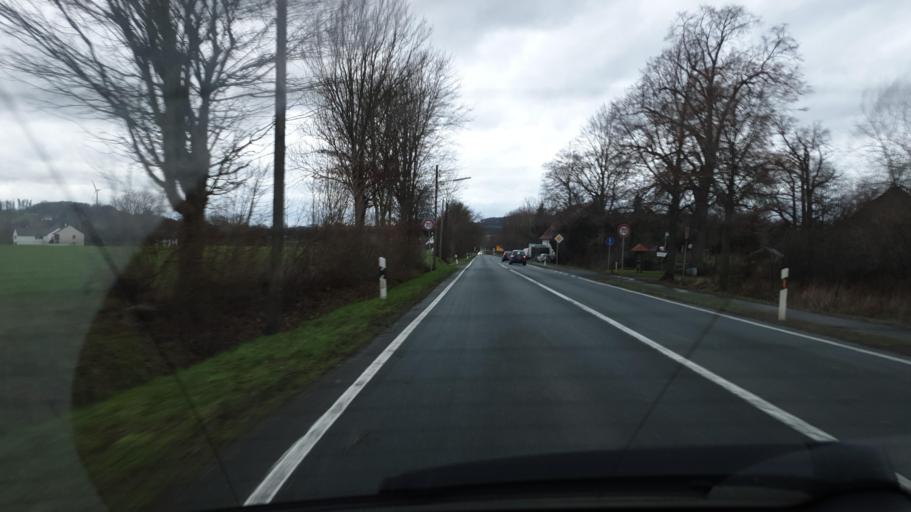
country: DE
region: North Rhine-Westphalia
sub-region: Regierungsbezirk Detmold
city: Vlotho
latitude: 52.1292
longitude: 8.8353
